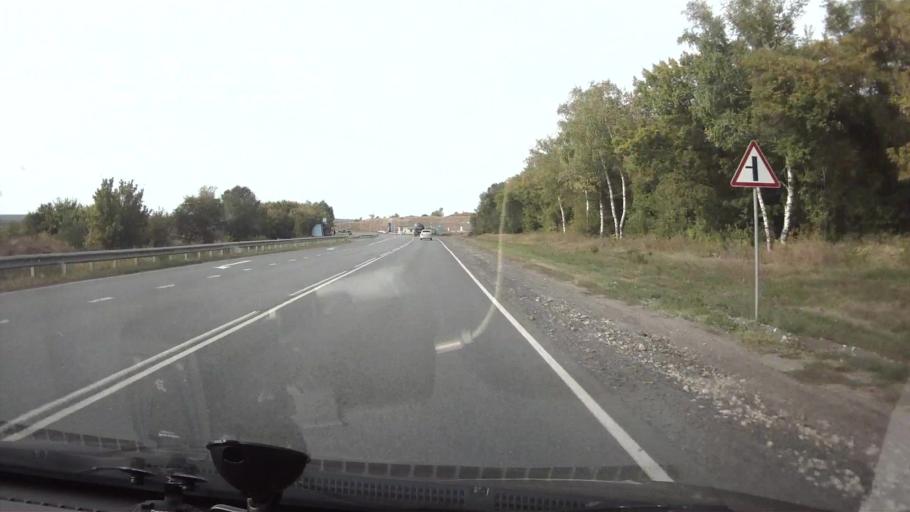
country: RU
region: Saratov
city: Tersa
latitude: 52.0908
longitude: 47.5451
